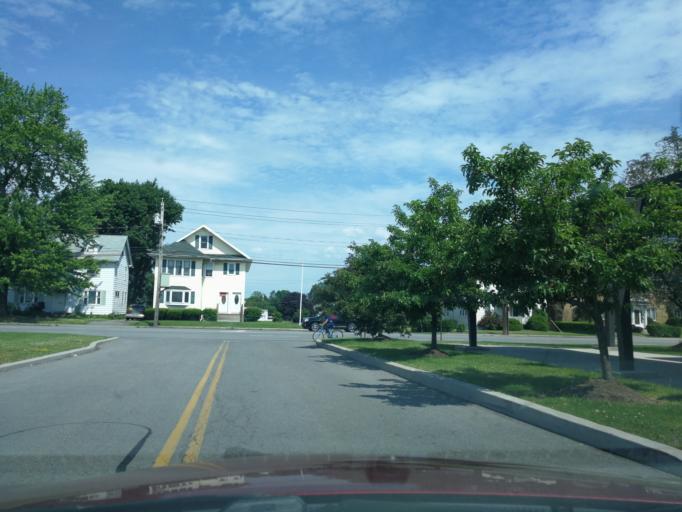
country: US
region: New York
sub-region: Monroe County
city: Irondequoit
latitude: 43.1899
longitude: -77.5848
